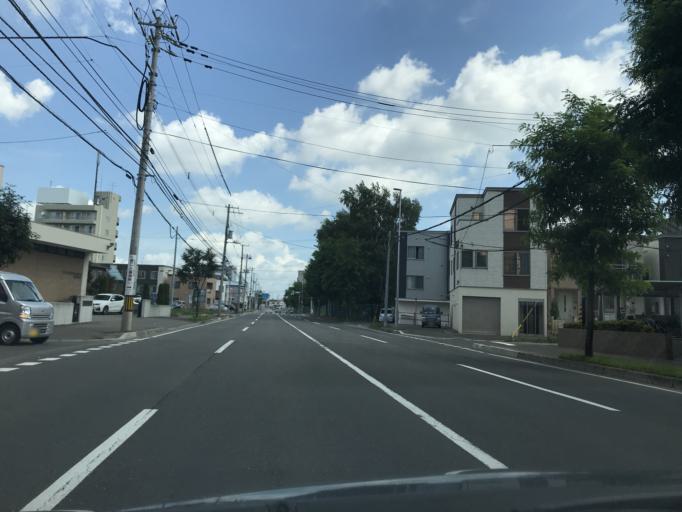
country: JP
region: Hokkaido
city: Sapporo
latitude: 43.0598
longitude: 141.3820
